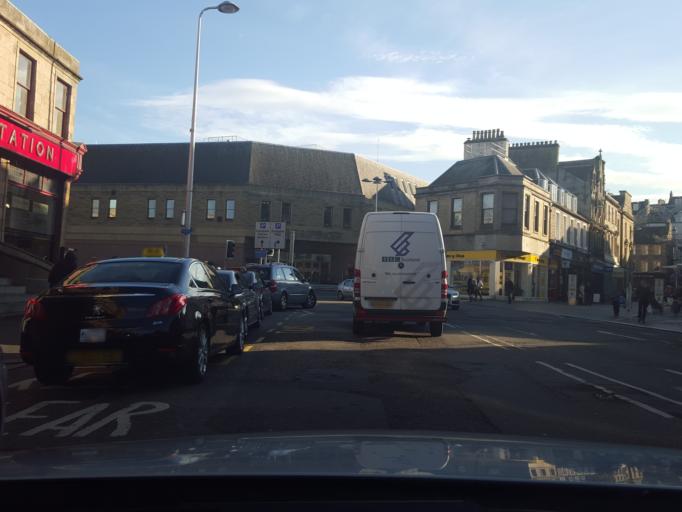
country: GB
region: Scotland
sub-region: Highland
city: Inverness
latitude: 57.4790
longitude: -4.2238
